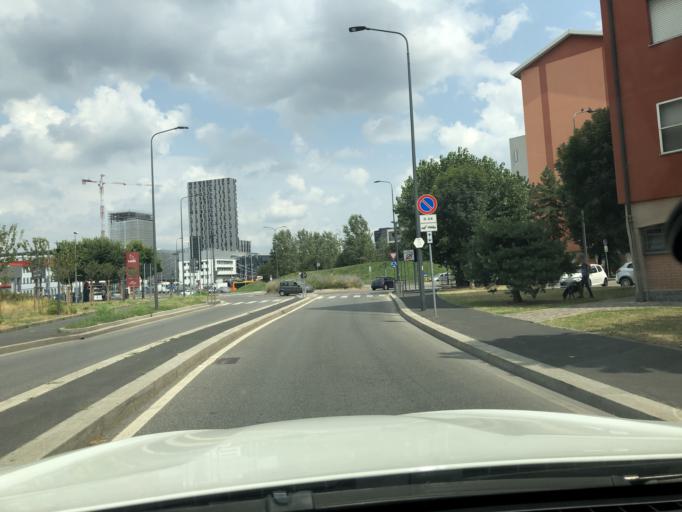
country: IT
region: Lombardy
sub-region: Citta metropolitana di Milano
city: Pero
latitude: 45.5056
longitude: 9.0965
